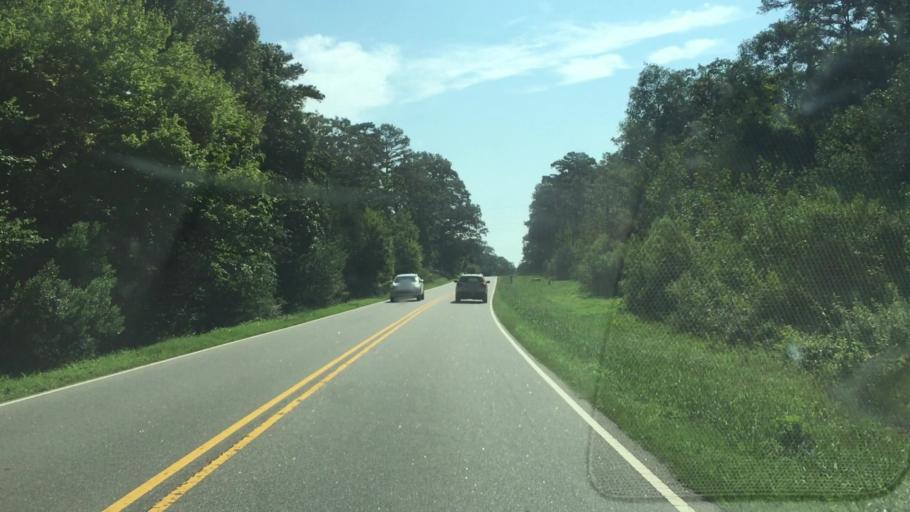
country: US
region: North Carolina
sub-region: Stanly County
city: Oakboro
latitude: 35.1346
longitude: -80.3804
